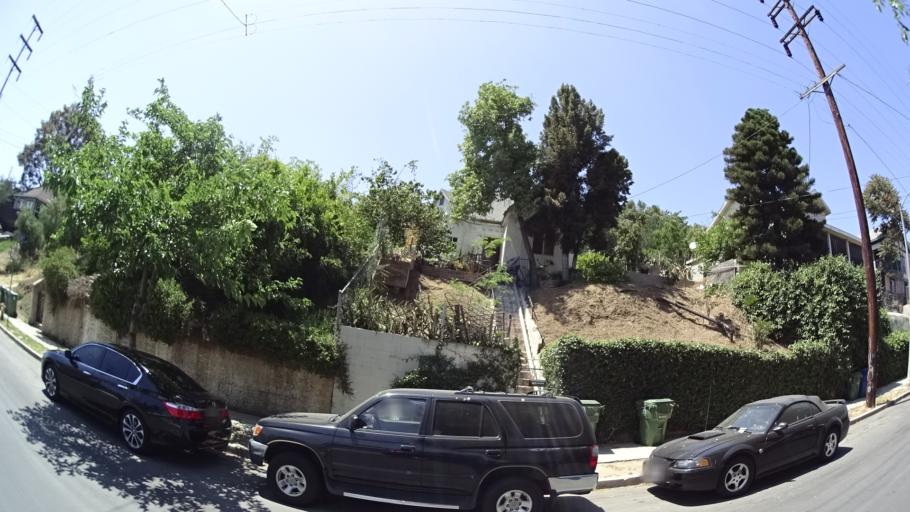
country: US
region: California
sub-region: Los Angeles County
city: Boyle Heights
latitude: 34.0775
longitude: -118.2040
